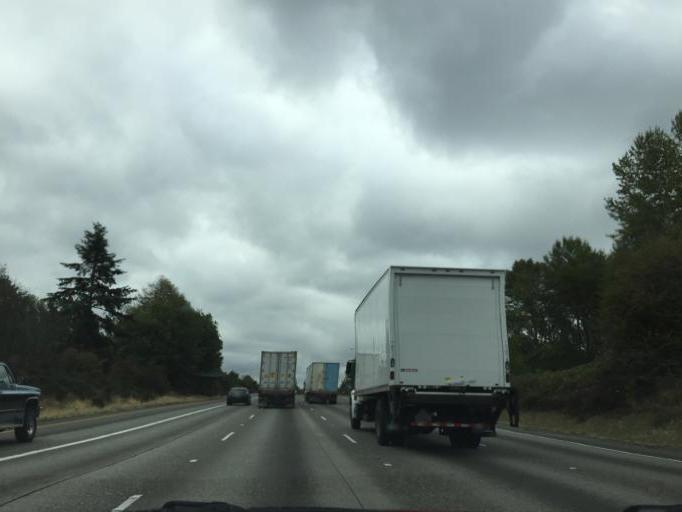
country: US
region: Washington
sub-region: King County
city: Lakeland North
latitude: 47.3634
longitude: -122.2954
